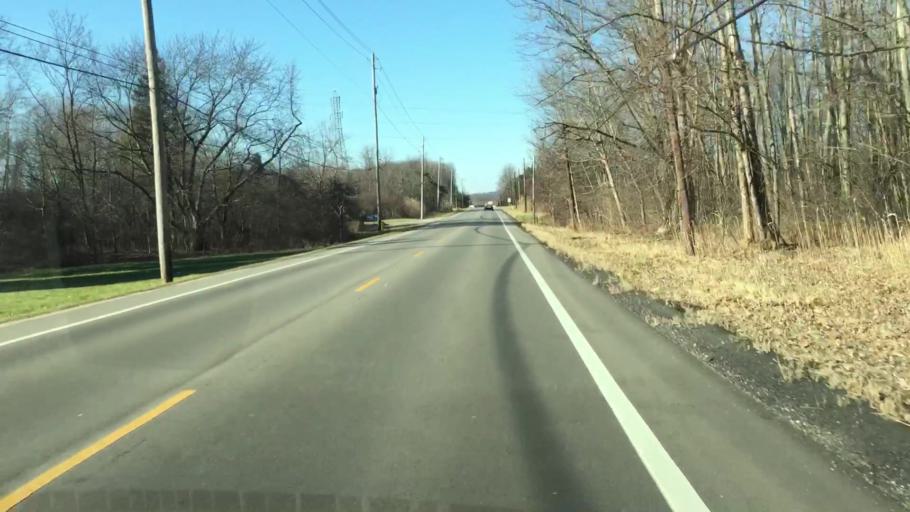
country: US
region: Ohio
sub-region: Summit County
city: Fairlawn
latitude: 41.0966
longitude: -81.6261
